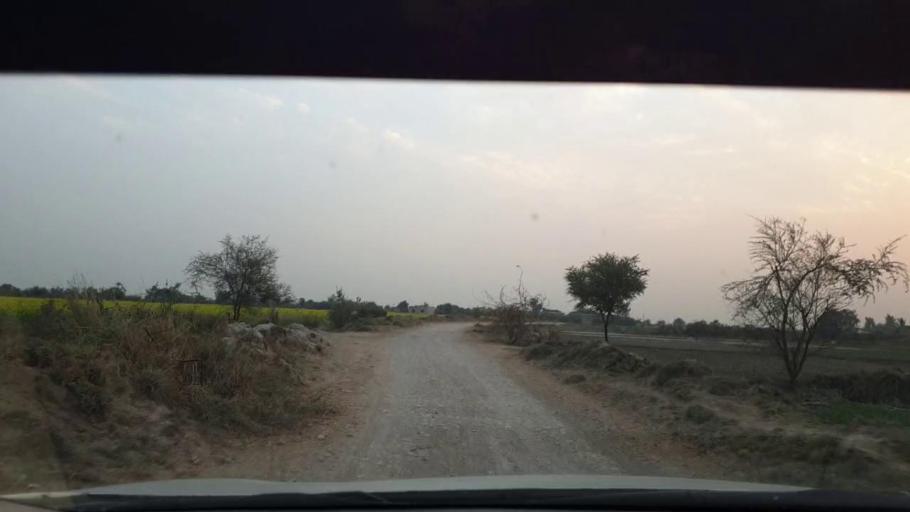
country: PK
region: Sindh
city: Berani
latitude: 25.8864
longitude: 68.7526
